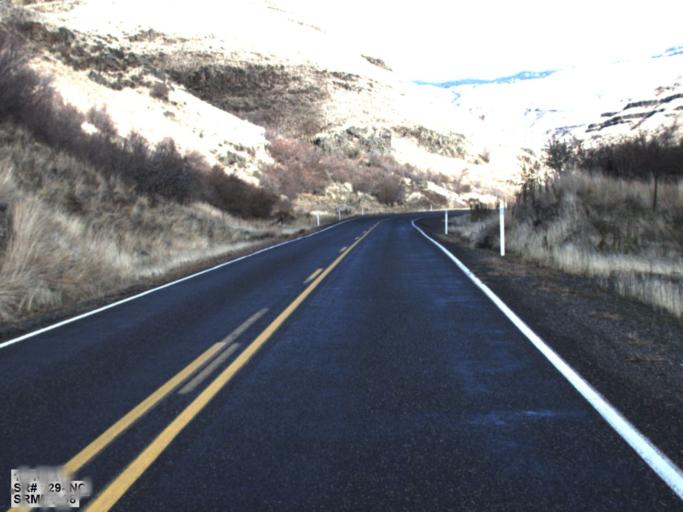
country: US
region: Washington
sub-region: Asotin County
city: Asotin
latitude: 46.0160
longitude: -117.2675
